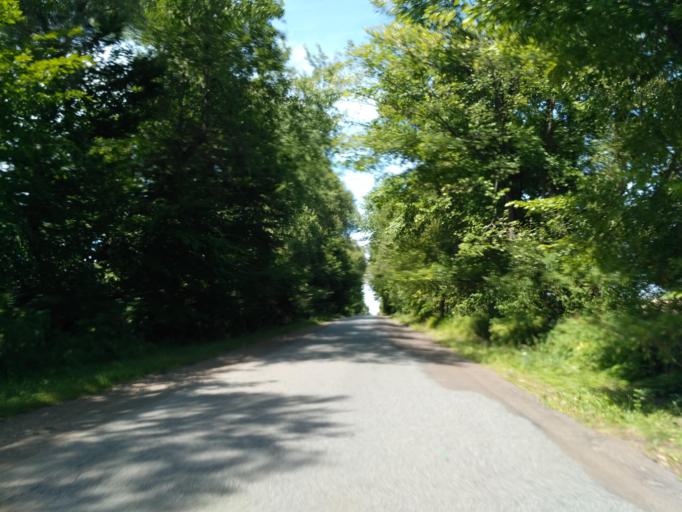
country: PL
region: Subcarpathian Voivodeship
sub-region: Powiat sanocki
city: Strachocina
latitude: 49.5726
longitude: 22.1214
